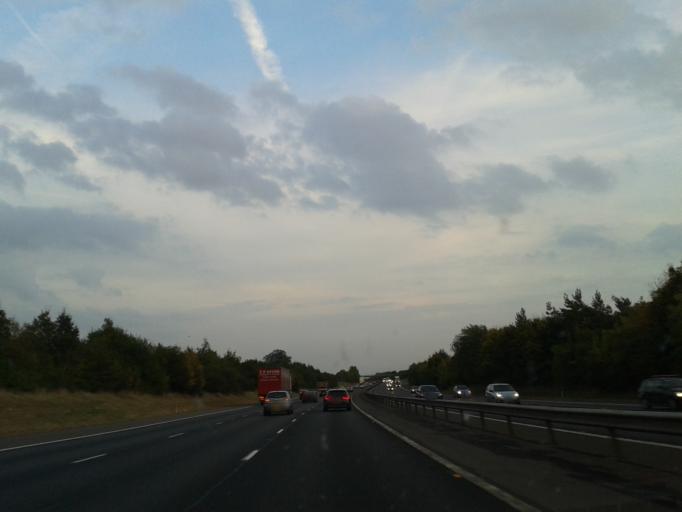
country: GB
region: England
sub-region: Warwickshire
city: Harbury
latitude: 52.2035
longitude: -1.4755
